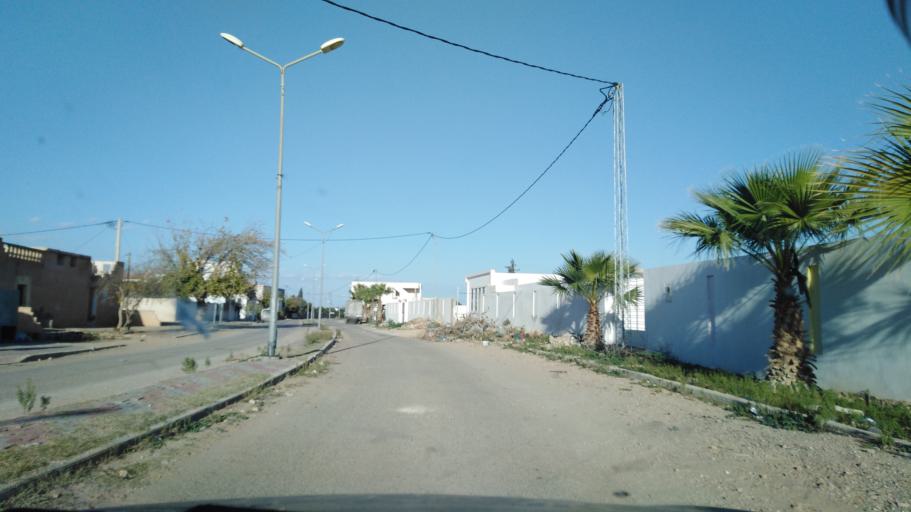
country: TN
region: Al Mahdiyah
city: Shurban
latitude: 34.9621
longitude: 10.3683
